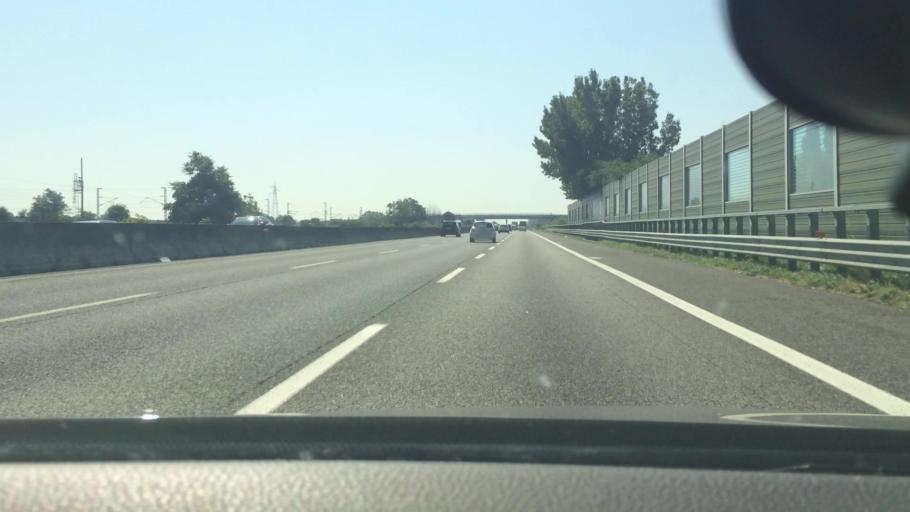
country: IT
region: Lombardy
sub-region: Provincia di Lodi
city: Pieve Fissiraga
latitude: 45.2673
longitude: 9.4614
